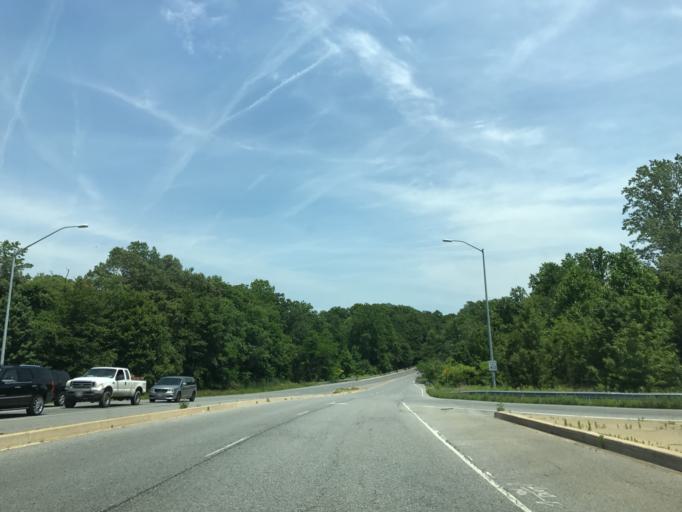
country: US
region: Maryland
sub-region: Anne Arundel County
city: South Gate
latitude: 39.0950
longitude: -76.6233
